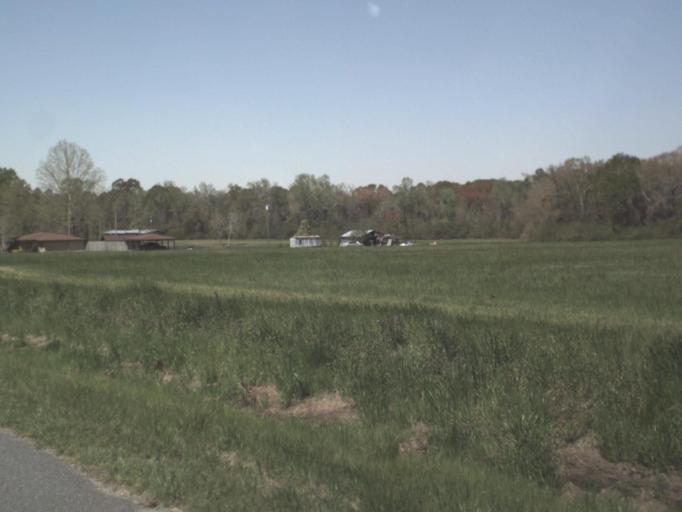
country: US
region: Florida
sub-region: Jackson County
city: Graceville
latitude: 30.9631
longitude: -85.5851
